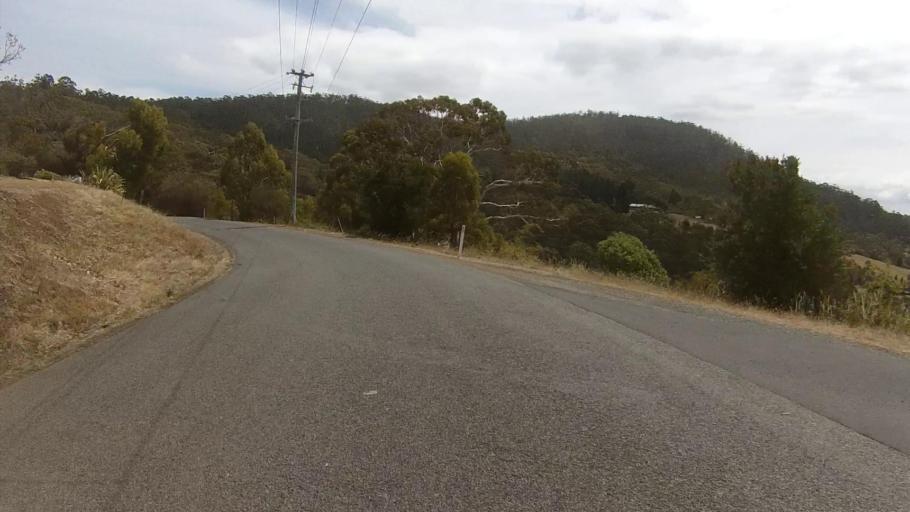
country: AU
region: Tasmania
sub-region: Kingborough
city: Blackmans Bay
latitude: -43.0450
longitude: 147.3375
